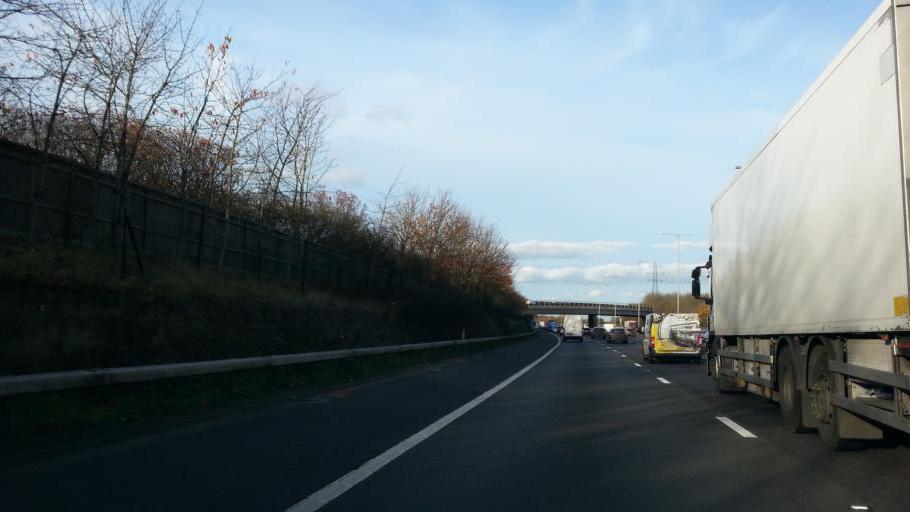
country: GB
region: England
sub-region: Buckinghamshire
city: Iver
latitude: 51.5195
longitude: -0.4991
